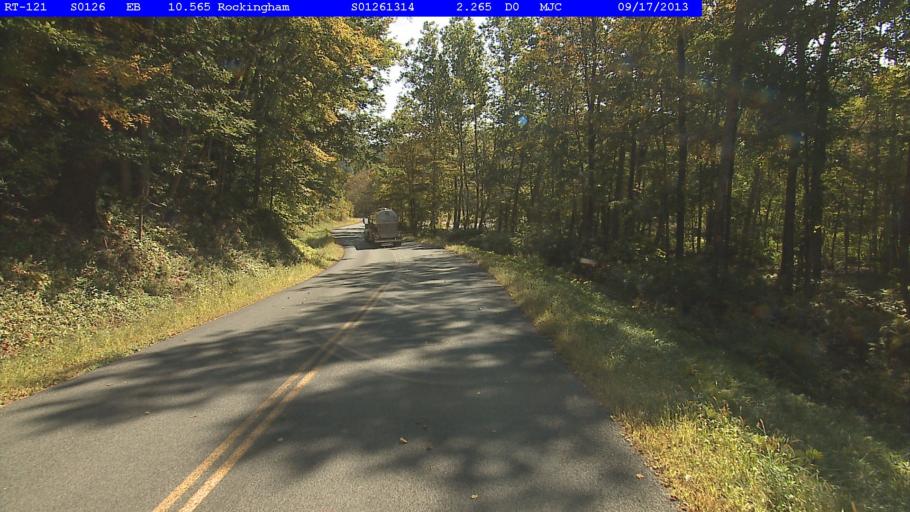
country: US
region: Vermont
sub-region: Windham County
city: Rockingham
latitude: 43.1353
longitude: -72.5204
